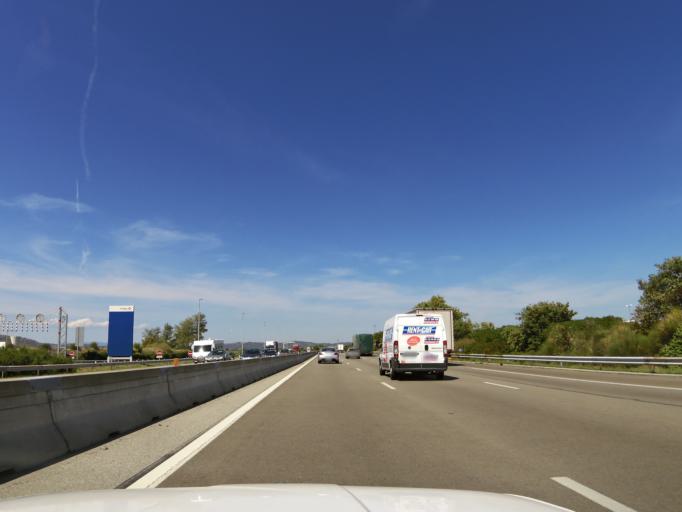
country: FR
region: Rhone-Alpes
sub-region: Departement de la Drome
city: La Roche-de-Glun
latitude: 45.0189
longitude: 4.8756
